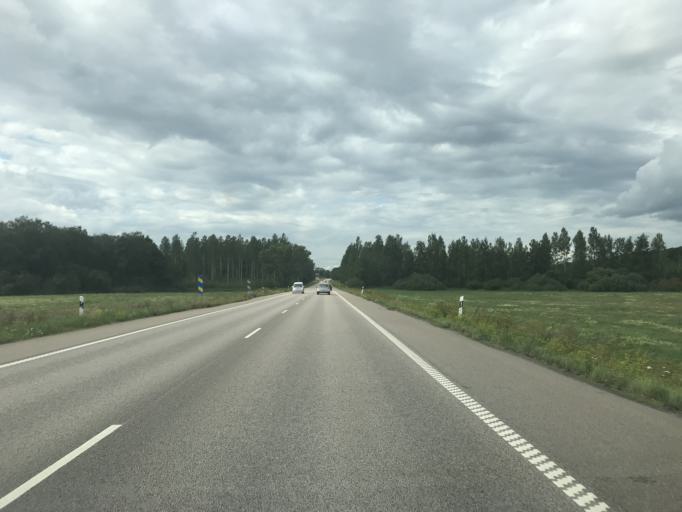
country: SE
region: Skane
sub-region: Hassleholms Kommun
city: Hassleholm
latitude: 56.1320
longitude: 13.8189
